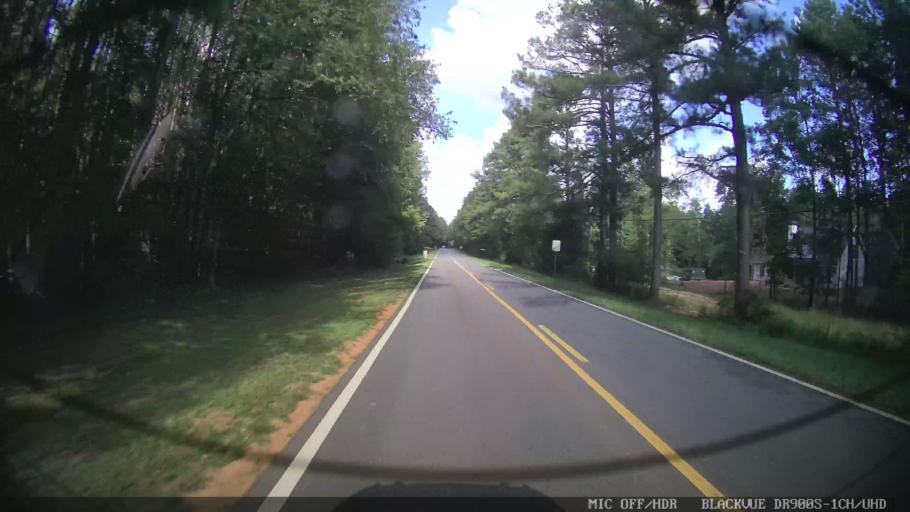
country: US
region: Georgia
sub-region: Bartow County
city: Euharlee
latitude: 34.1773
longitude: -85.0066
